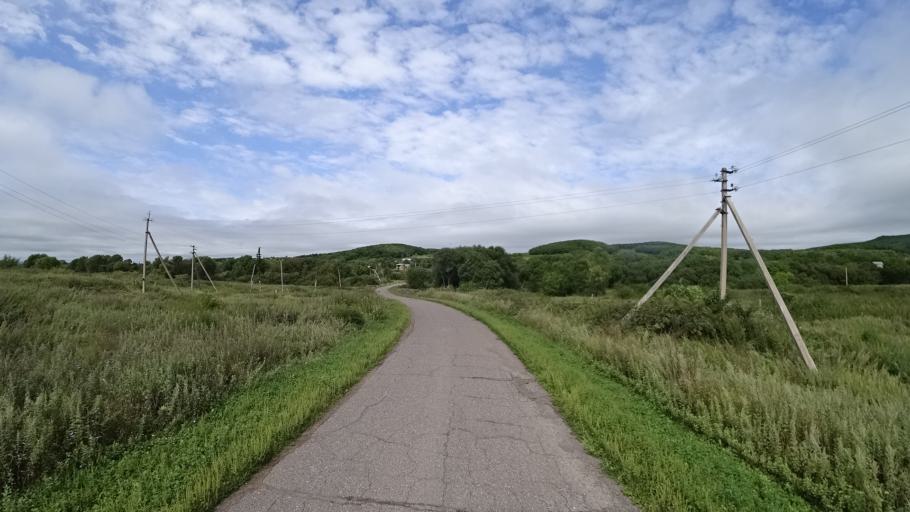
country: RU
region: Primorskiy
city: Lyalichi
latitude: 44.1346
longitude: 132.3879
